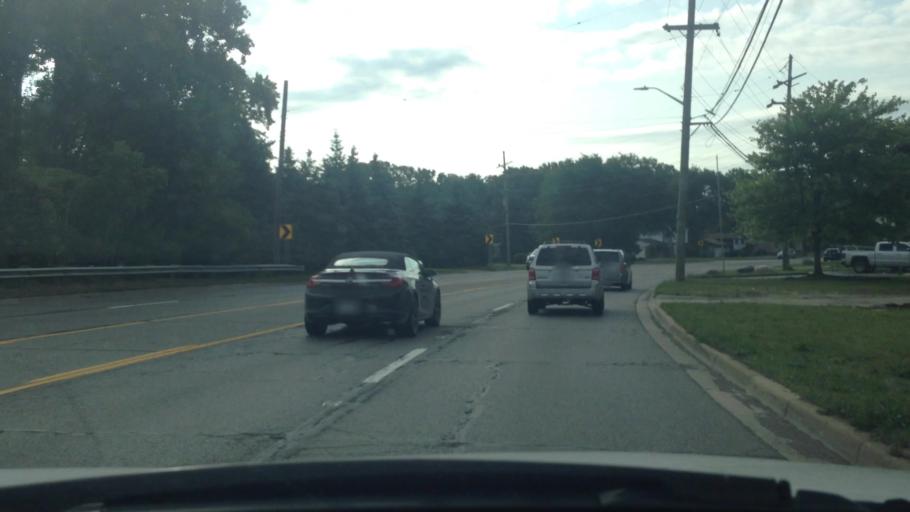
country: US
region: Michigan
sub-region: Oakland County
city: Waterford
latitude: 42.6869
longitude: -83.3459
